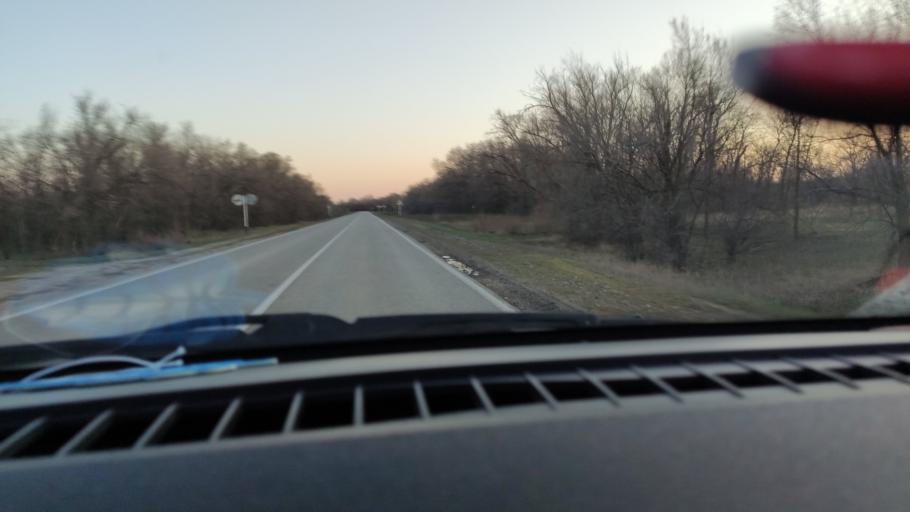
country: RU
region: Saratov
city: Privolzhskiy
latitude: 51.2725
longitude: 45.9475
